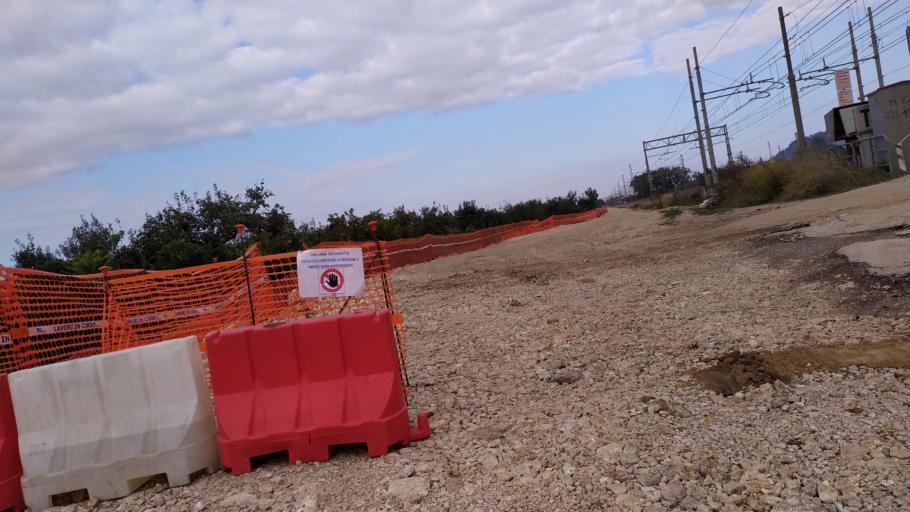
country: IT
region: Campania
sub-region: Provincia di Caserta
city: Montedecoro
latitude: 41.0190
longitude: 14.4044
